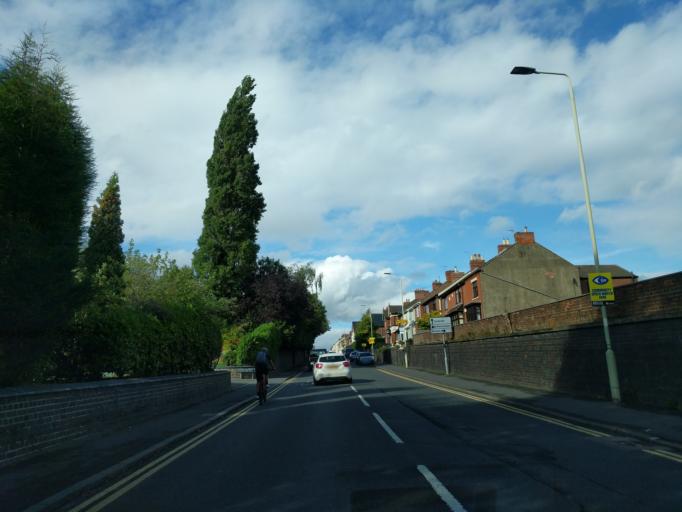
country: GB
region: England
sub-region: Leicestershire
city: Coalville
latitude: 52.7101
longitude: -1.3717
